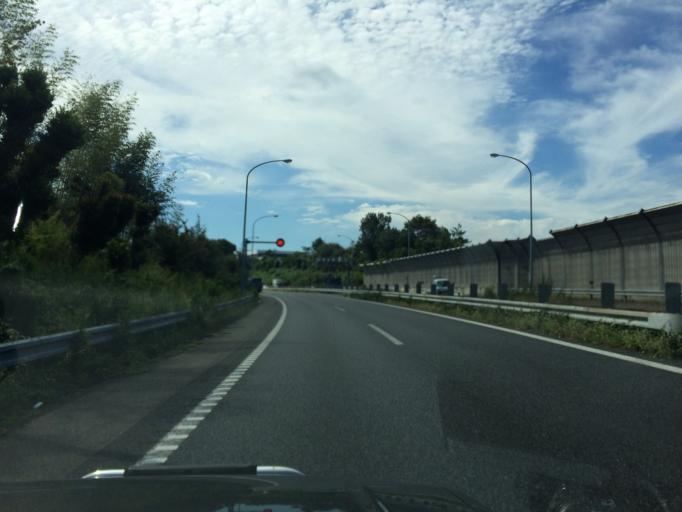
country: JP
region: Osaka
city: Izumi
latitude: 34.4549
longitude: 135.4463
